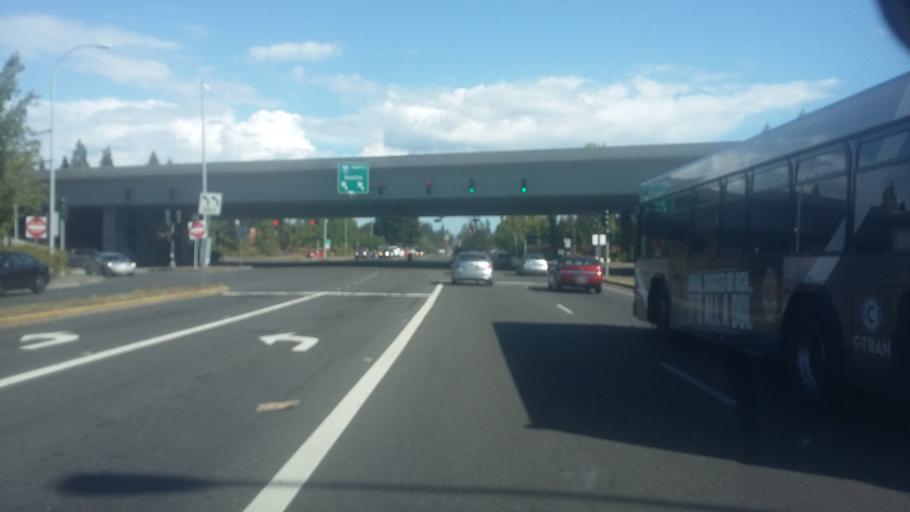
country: US
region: Washington
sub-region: Clark County
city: Hazel Dell
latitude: 45.6929
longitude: -122.6625
